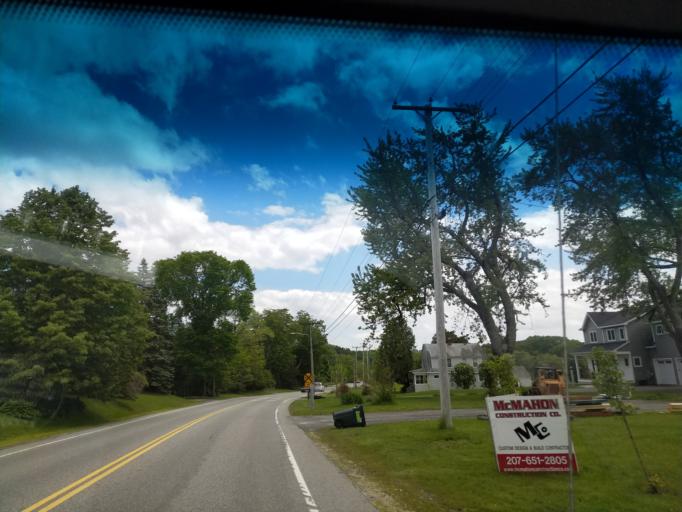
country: US
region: Maine
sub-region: Cumberland County
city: Falmouth
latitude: 43.7417
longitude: -70.2896
